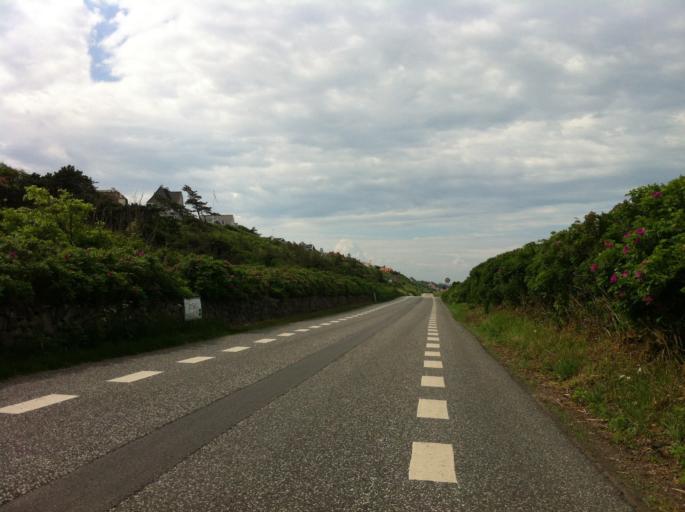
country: DK
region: Capital Region
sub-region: Gribskov Kommune
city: Helsinge
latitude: 56.1041
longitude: 12.1720
